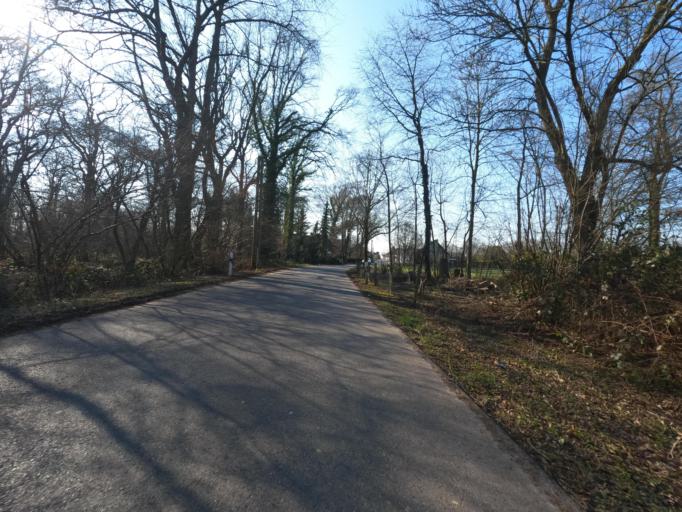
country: DE
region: North Rhine-Westphalia
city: Erkelenz
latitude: 51.0541
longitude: 6.3204
